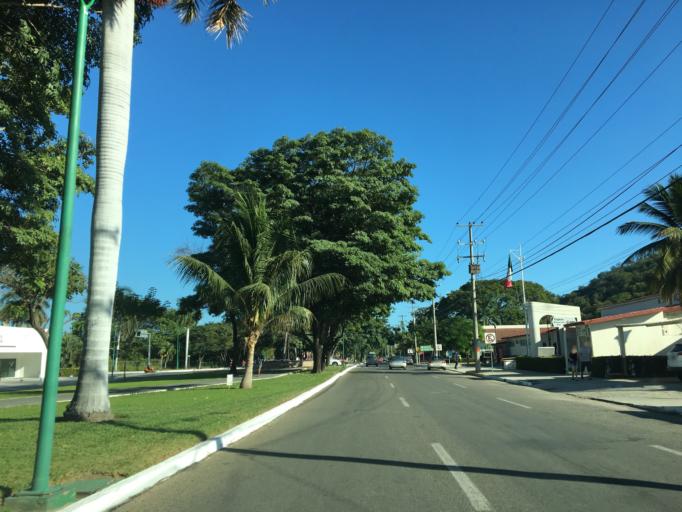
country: MX
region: Oaxaca
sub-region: Santa Maria Huatulco
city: Crucecita
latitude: 15.7642
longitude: -96.1336
